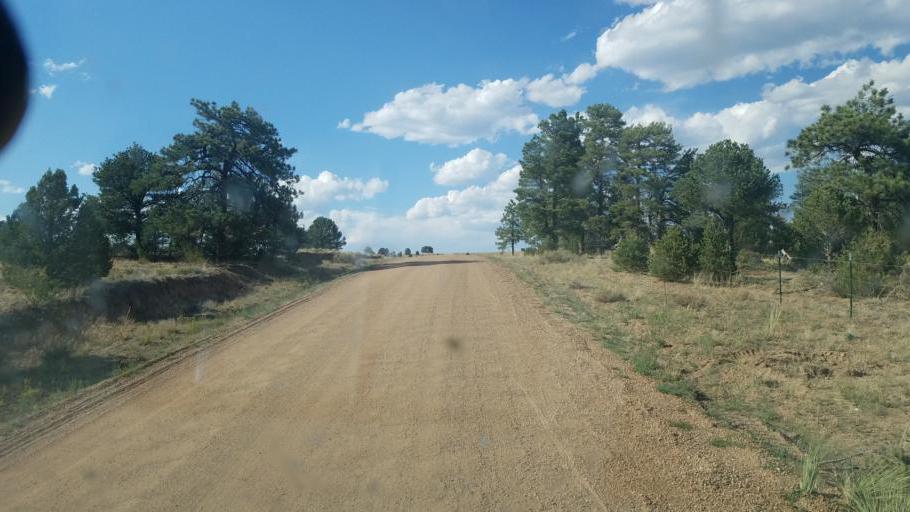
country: US
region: Colorado
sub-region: Custer County
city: Westcliffe
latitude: 38.2852
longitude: -105.4774
